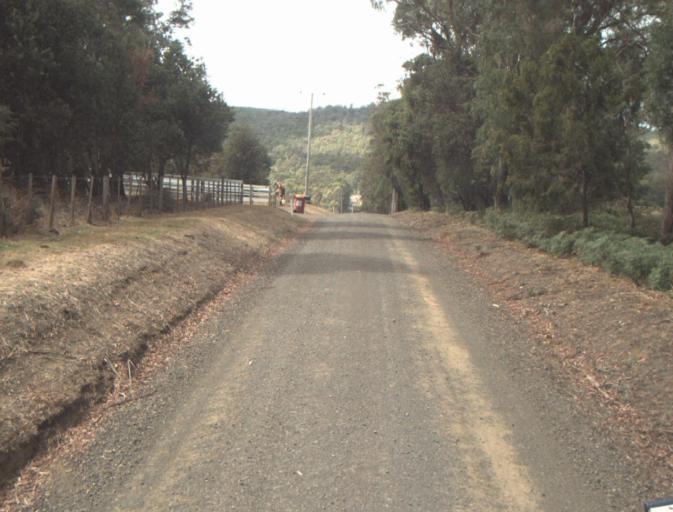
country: AU
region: Tasmania
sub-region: Launceston
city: Mayfield
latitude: -41.2803
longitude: 147.0435
